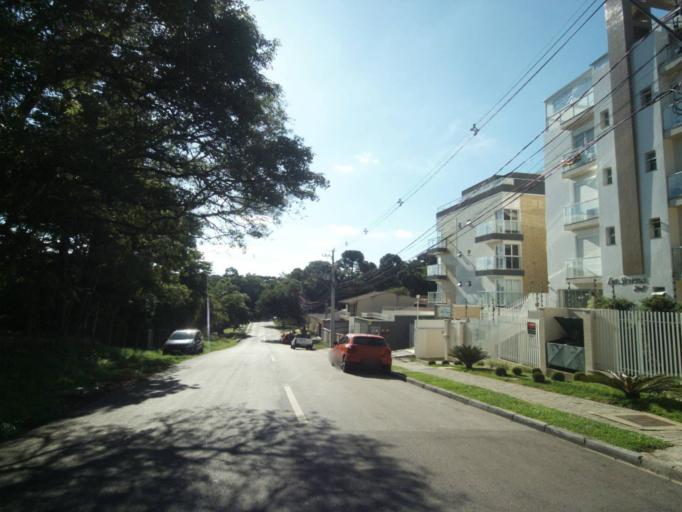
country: BR
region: Parana
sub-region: Curitiba
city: Curitiba
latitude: -25.4451
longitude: -49.3219
